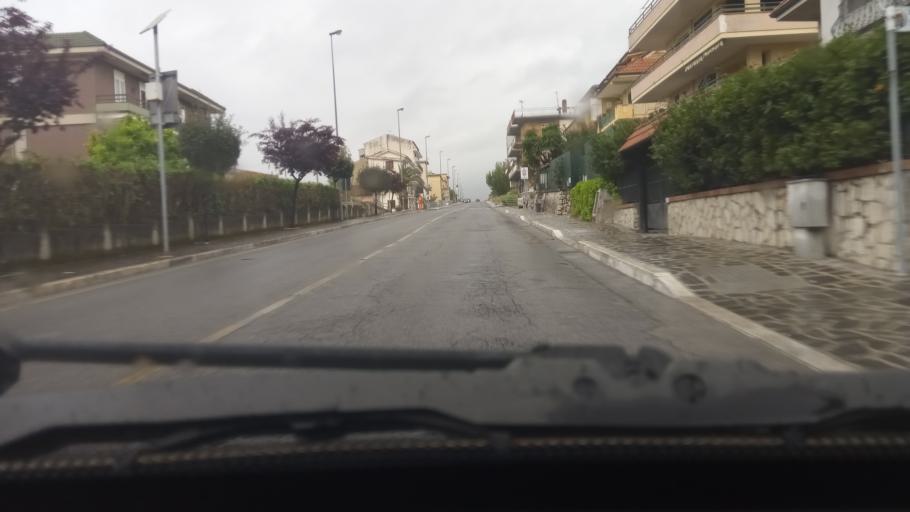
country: IT
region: Latium
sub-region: Provincia di Latina
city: Penitro
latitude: 41.2587
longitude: 13.6986
